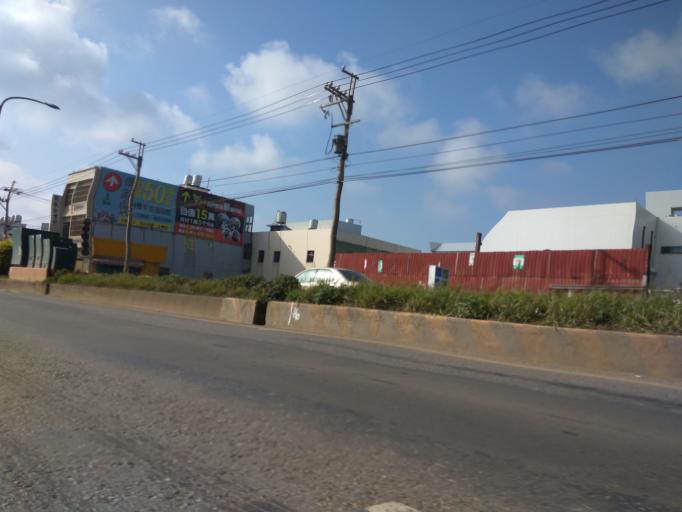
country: TW
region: Taiwan
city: Taoyuan City
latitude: 25.0674
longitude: 121.1882
